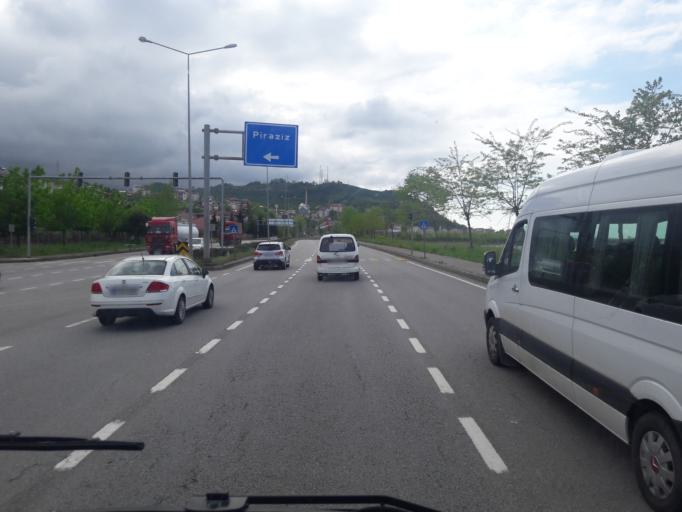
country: TR
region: Giresun
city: Piraziz
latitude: 40.9534
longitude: 38.1292
